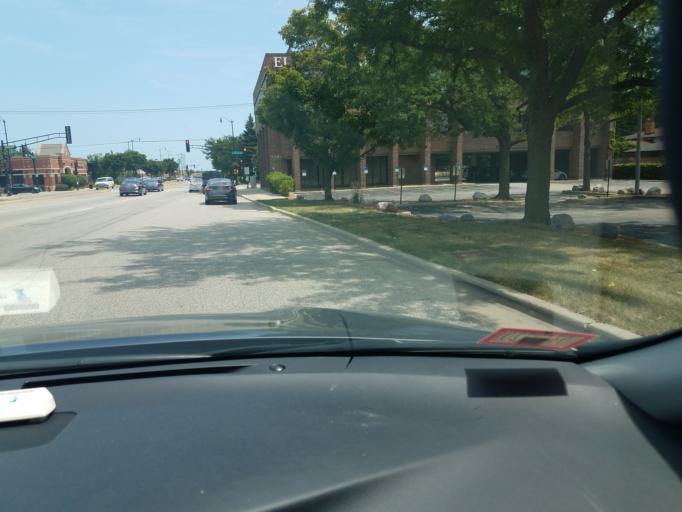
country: US
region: Illinois
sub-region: Cook County
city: Morton Grove
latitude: 42.0408
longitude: -87.7603
